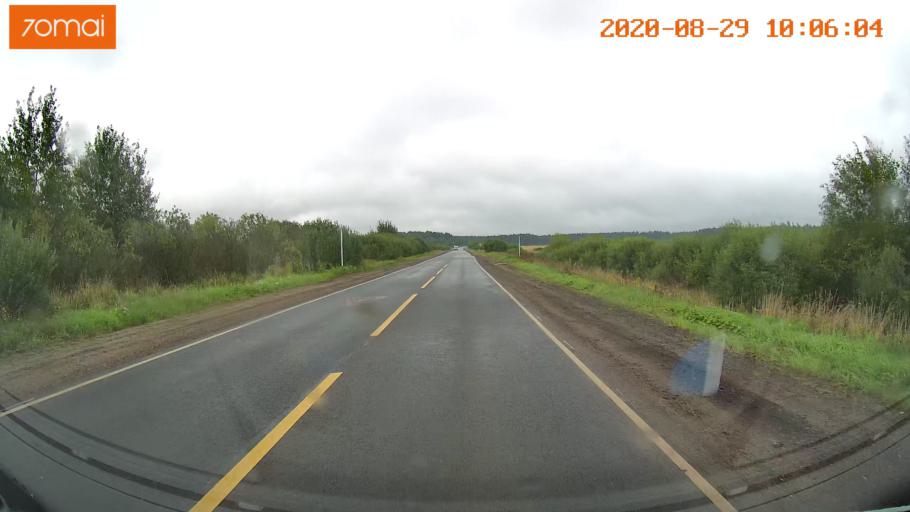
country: RU
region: Ivanovo
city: Zarechnyy
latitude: 57.3902
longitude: 42.5371
